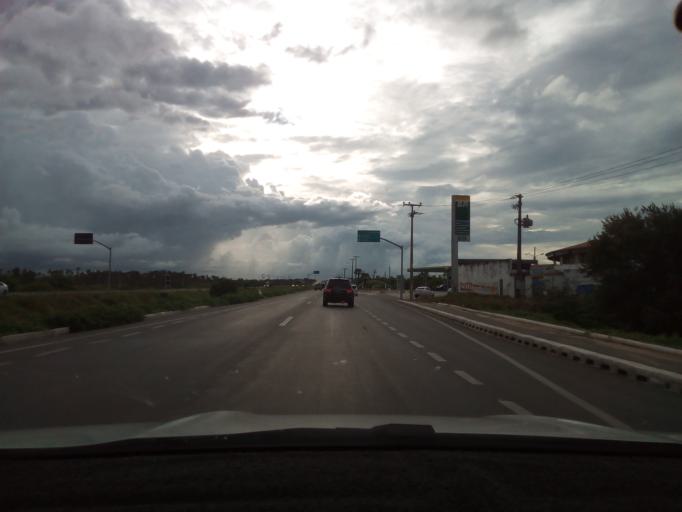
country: BR
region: Ceara
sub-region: Aracati
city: Aracati
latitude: -4.5793
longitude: -37.7779
